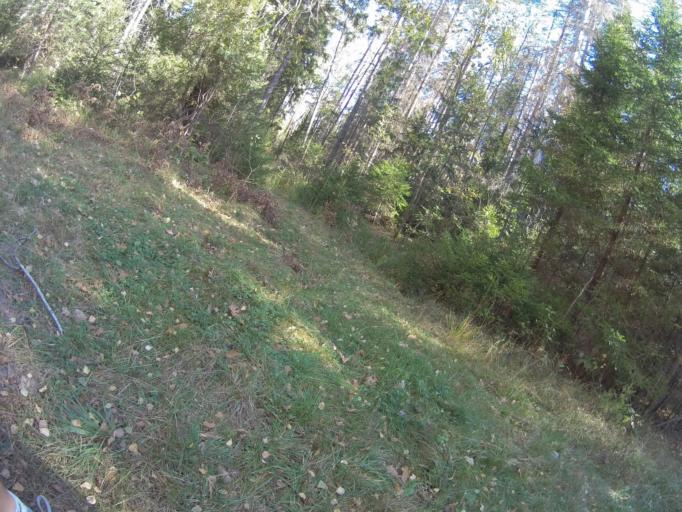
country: RU
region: Vladimir
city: Golovino
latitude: 56.0265
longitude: 40.4899
